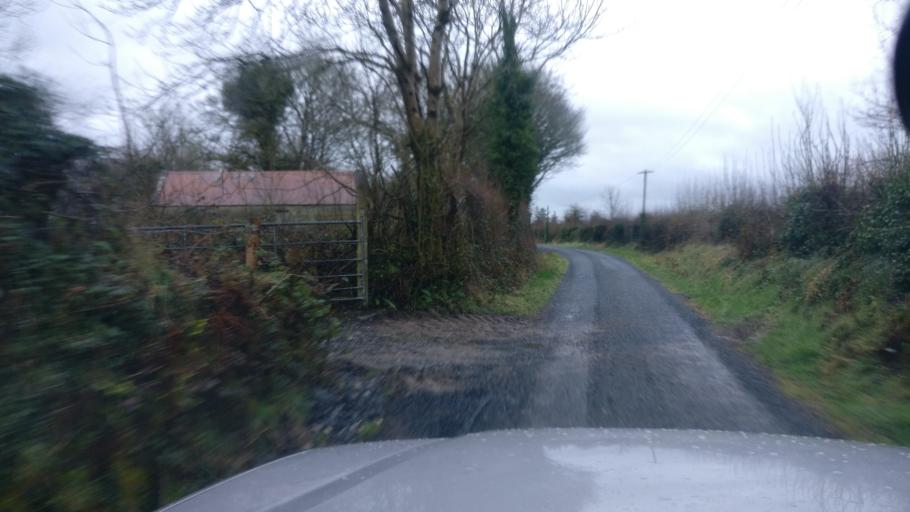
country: IE
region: Connaught
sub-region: County Galway
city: Ballinasloe
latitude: 53.2522
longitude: -8.3597
